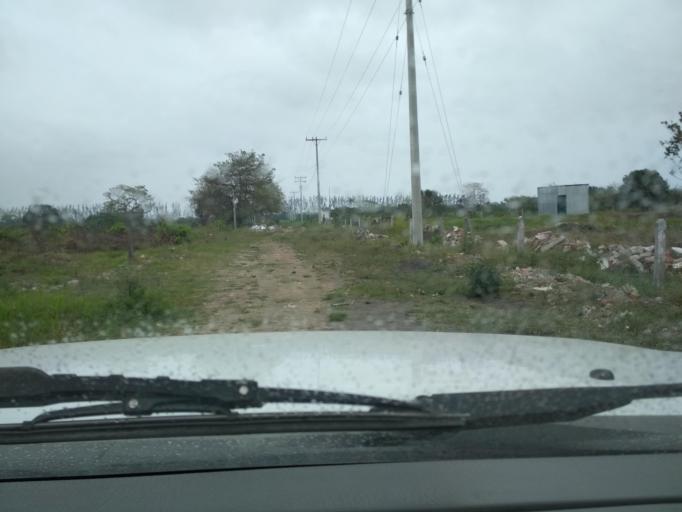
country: MX
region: Veracruz
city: Paso del Toro
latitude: 19.0436
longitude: -96.1316
